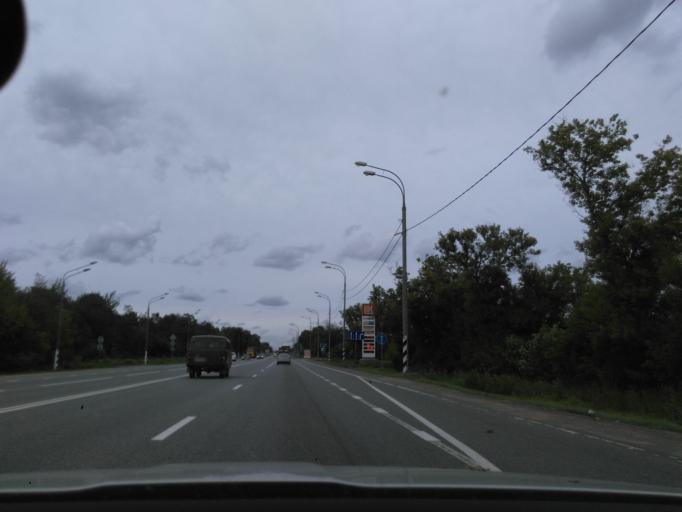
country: RU
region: Moskovskaya
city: Klin
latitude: 56.3078
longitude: 36.7831
